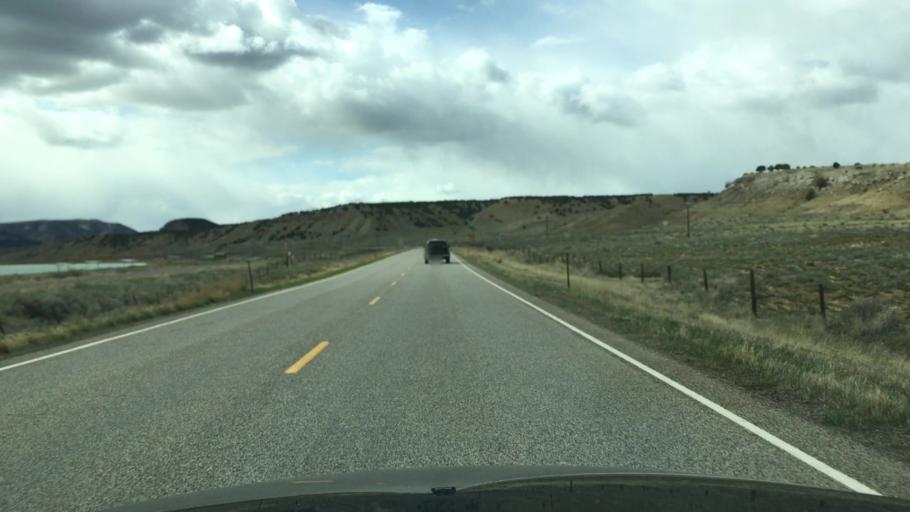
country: US
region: Colorado
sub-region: Rio Blanco County
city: Meeker
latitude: 40.0898
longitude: -108.2045
